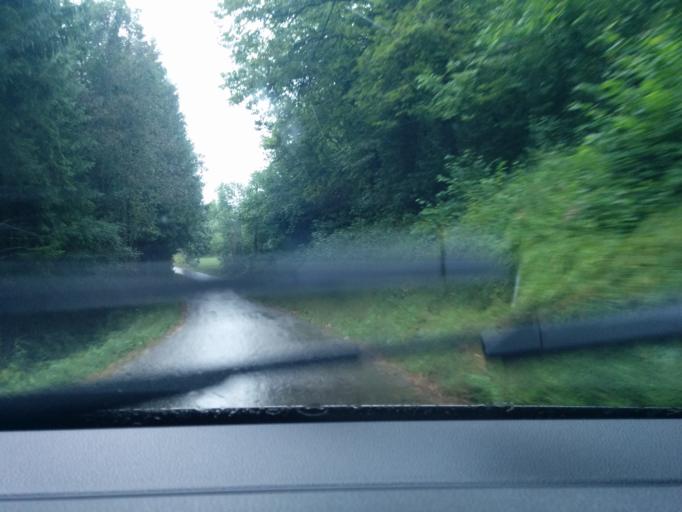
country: FR
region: Franche-Comte
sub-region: Departement du Jura
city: Valfin-les-Saint-Claude
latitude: 46.4619
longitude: 5.8386
